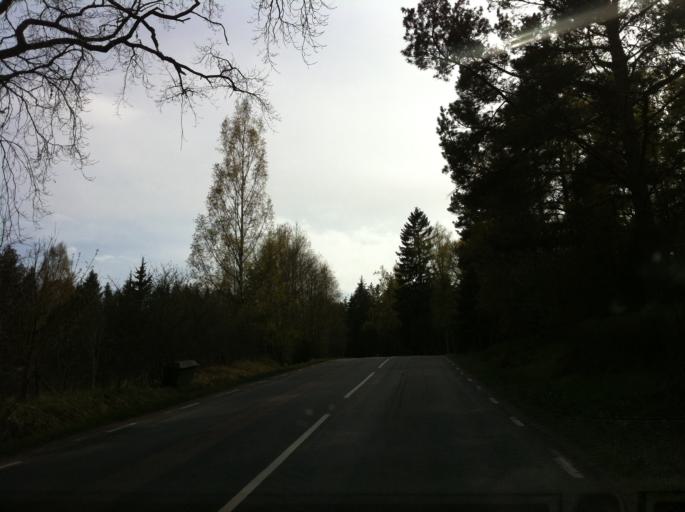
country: SE
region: Soedermanland
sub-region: Nykopings Kommun
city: Olstorp
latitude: 58.7341
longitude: 16.6957
